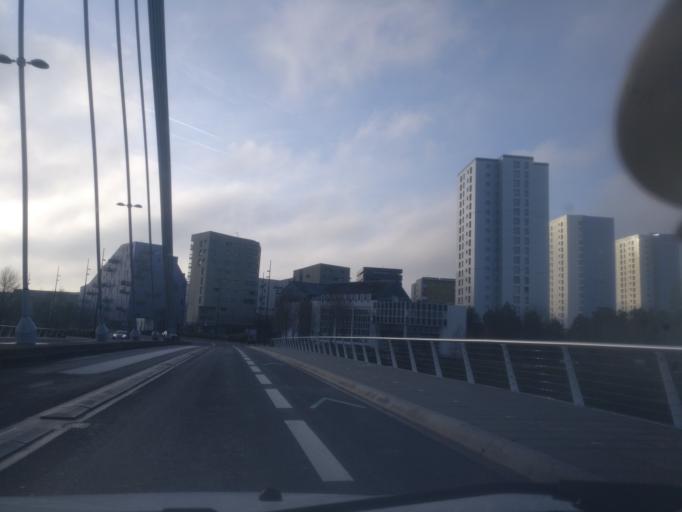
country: FR
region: Pays de la Loire
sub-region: Departement de la Loire-Atlantique
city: Nantes
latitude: 47.2122
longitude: -1.5292
